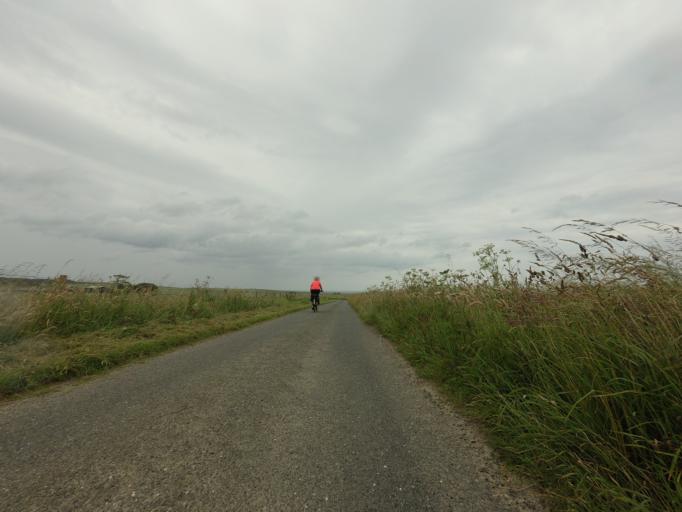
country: GB
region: Scotland
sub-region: Moray
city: Cullen
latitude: 57.6653
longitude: -2.7617
